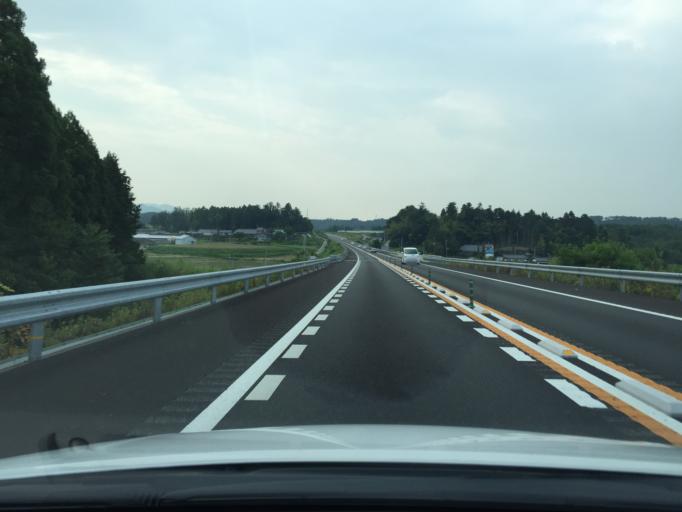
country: JP
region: Fukushima
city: Namie
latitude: 37.5717
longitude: 140.9429
